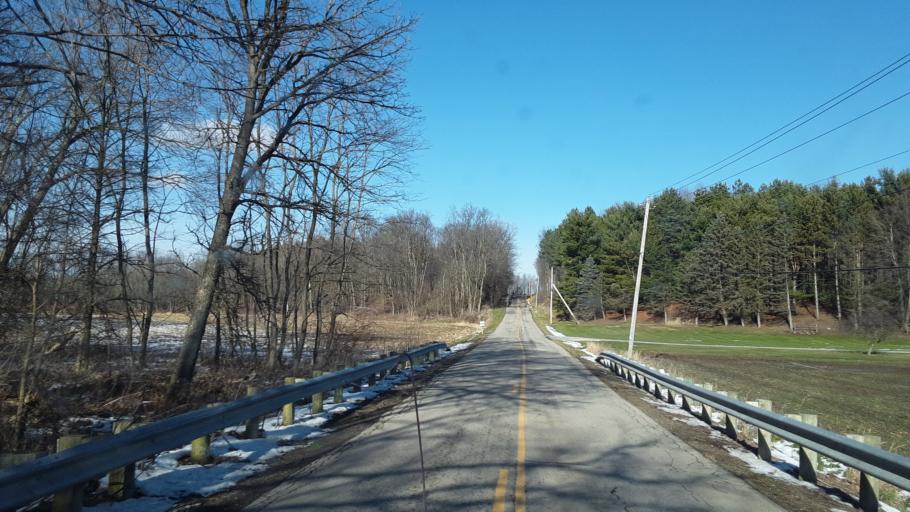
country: US
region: Ohio
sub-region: Richland County
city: Lincoln Heights
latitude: 40.8492
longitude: -82.4795
